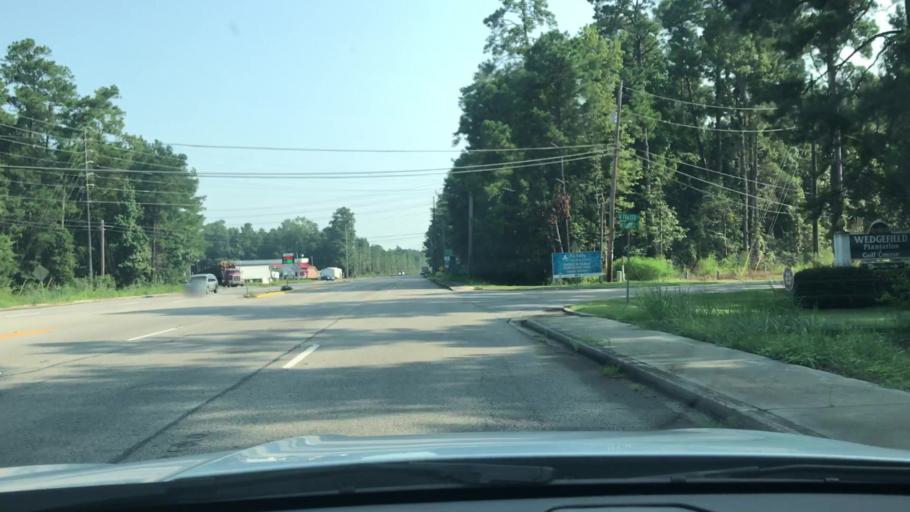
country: US
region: South Carolina
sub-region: Georgetown County
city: Georgetown
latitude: 33.4155
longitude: -79.2844
